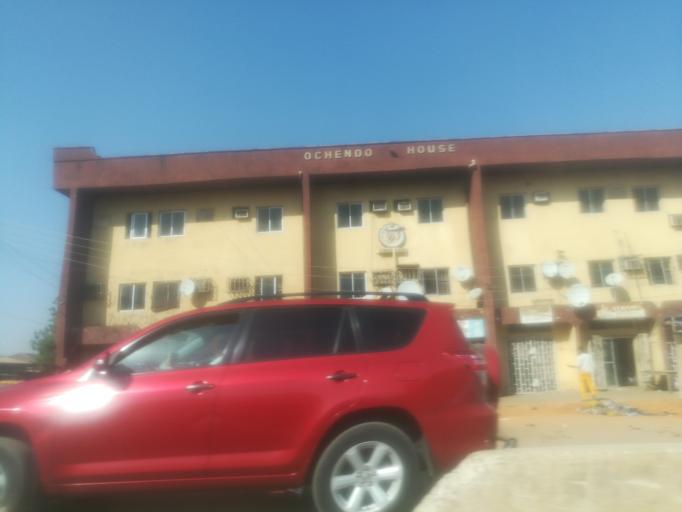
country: NG
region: Kano
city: Kano
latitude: 12.0251
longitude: 8.5346
